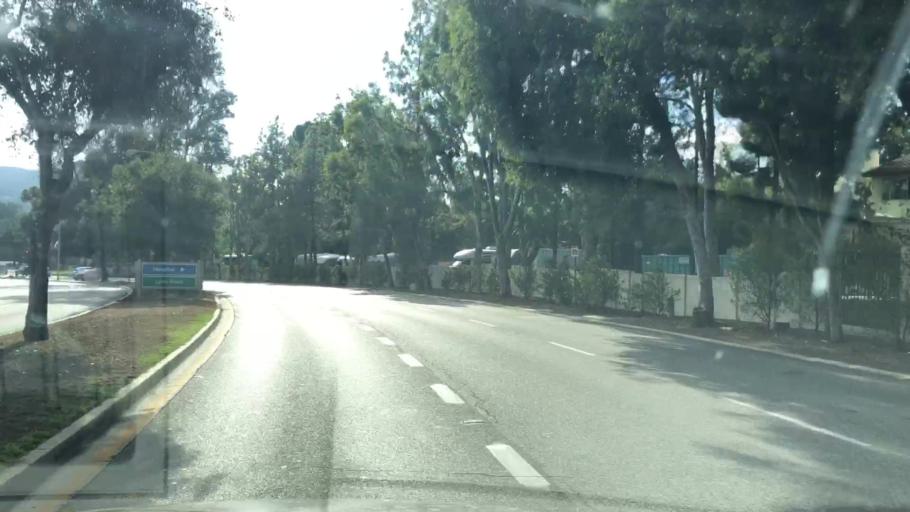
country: US
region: California
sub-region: Ventura County
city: Casa Conejo
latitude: 34.1875
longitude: -118.8906
